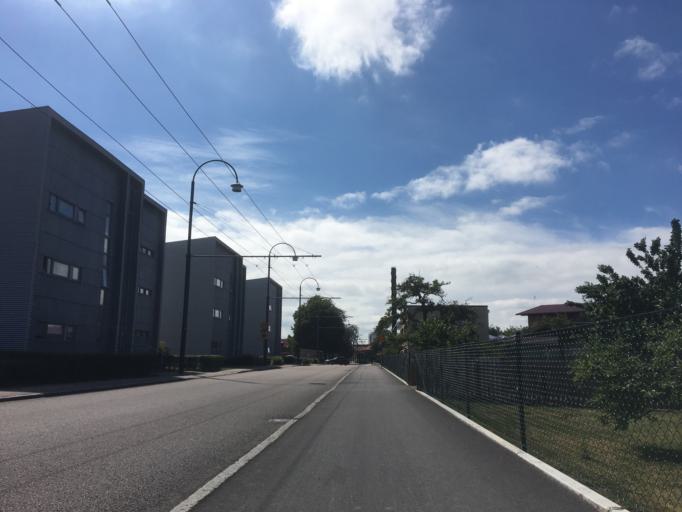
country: SE
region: Skane
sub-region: Landskrona
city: Landskrona
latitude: 55.8793
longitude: 12.8436
